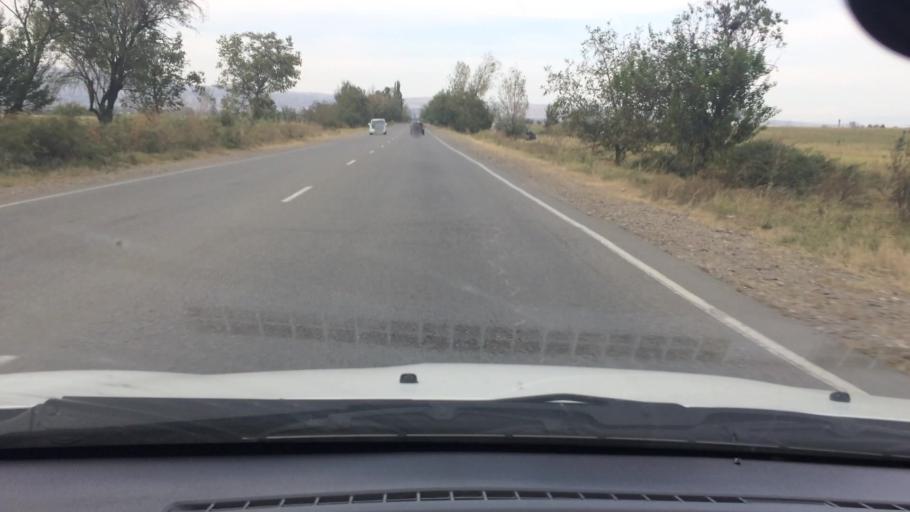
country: GE
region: Kvemo Kartli
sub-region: Marneuli
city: Marneuli
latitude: 41.5485
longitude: 44.7765
